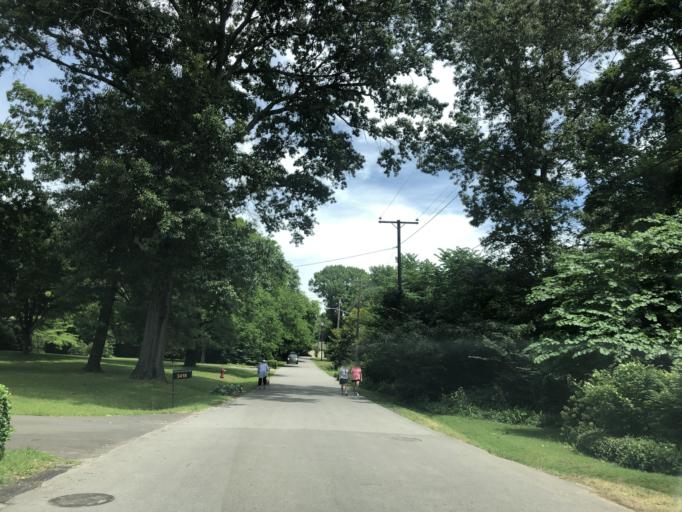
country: US
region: Tennessee
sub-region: Davidson County
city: Oak Hill
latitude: 36.1156
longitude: -86.8029
